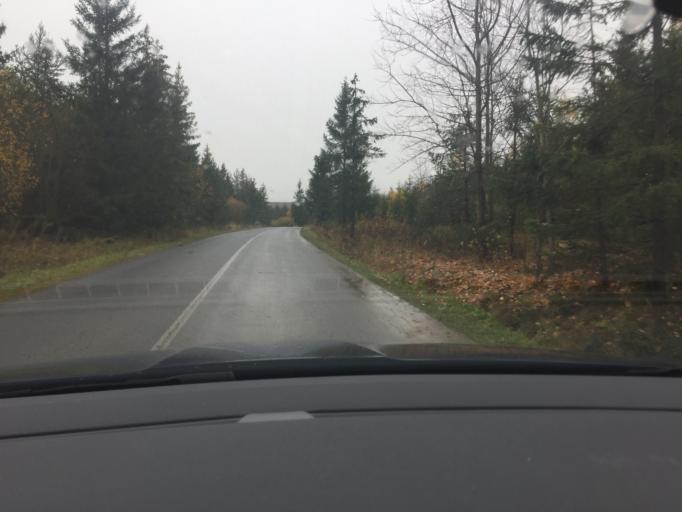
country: SK
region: Presovsky
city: Spisska Bela
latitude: 49.2067
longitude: 20.3730
